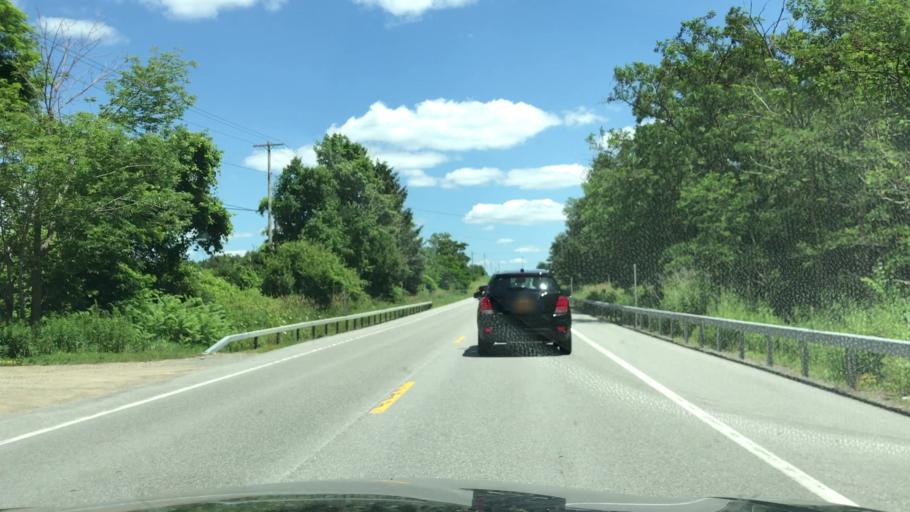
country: US
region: New York
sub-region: Wyoming County
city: Attica
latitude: 42.7706
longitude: -78.3558
